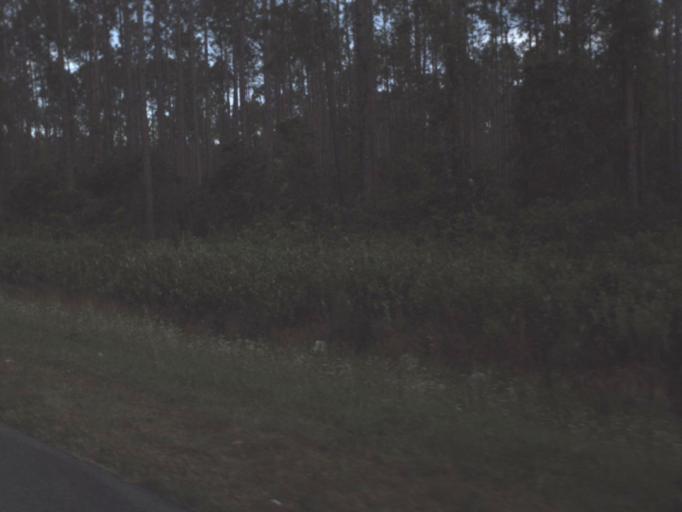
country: US
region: Florida
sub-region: Marion County
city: Silver Springs Shores
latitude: 29.2123
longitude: -81.9524
